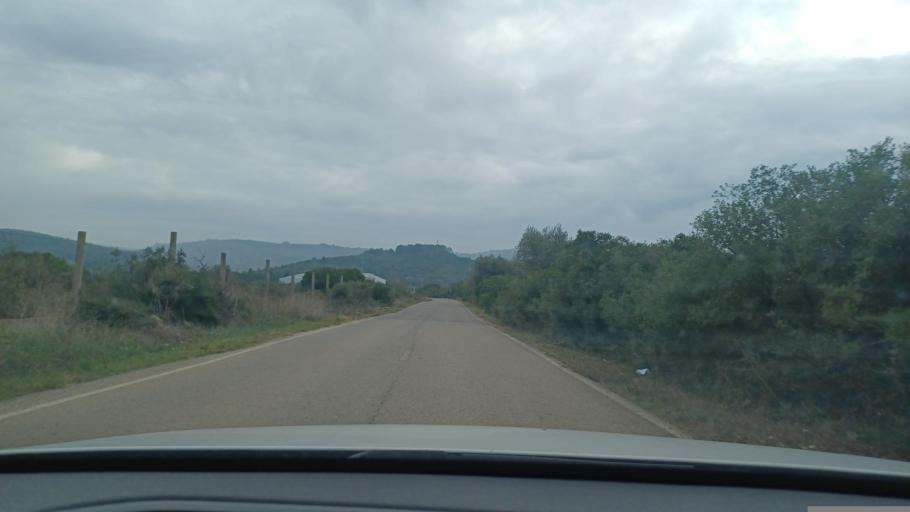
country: ES
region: Catalonia
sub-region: Provincia de Tarragona
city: Santa Barbara
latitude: 40.6628
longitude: 0.4590
